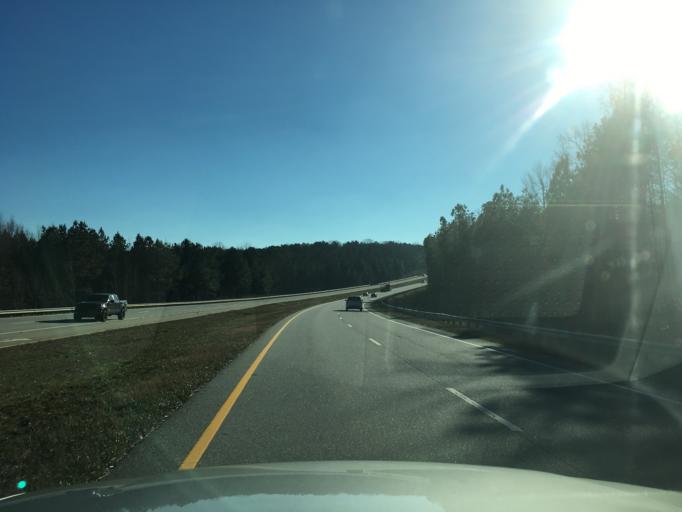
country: US
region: Georgia
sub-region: Carroll County
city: Carrollton
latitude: 33.4498
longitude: -85.1247
